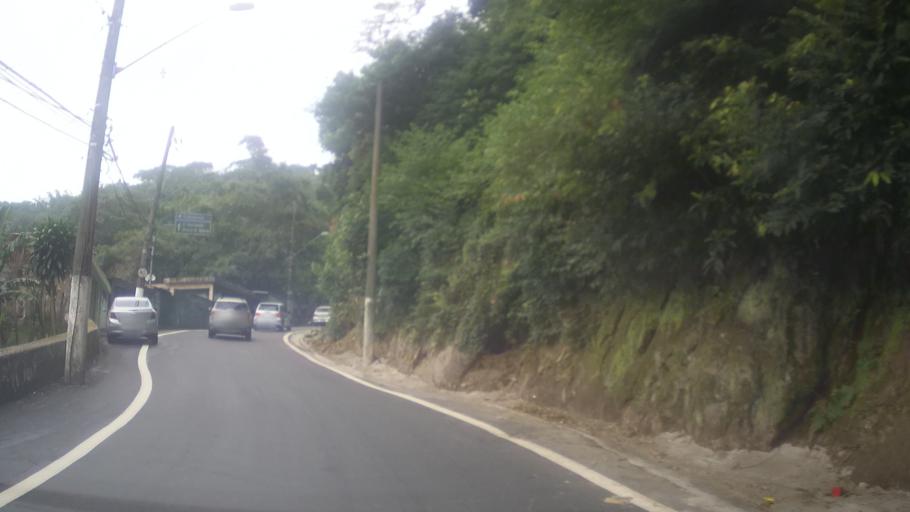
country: BR
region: Sao Paulo
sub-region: Santos
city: Santos
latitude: -23.9417
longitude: -46.3442
